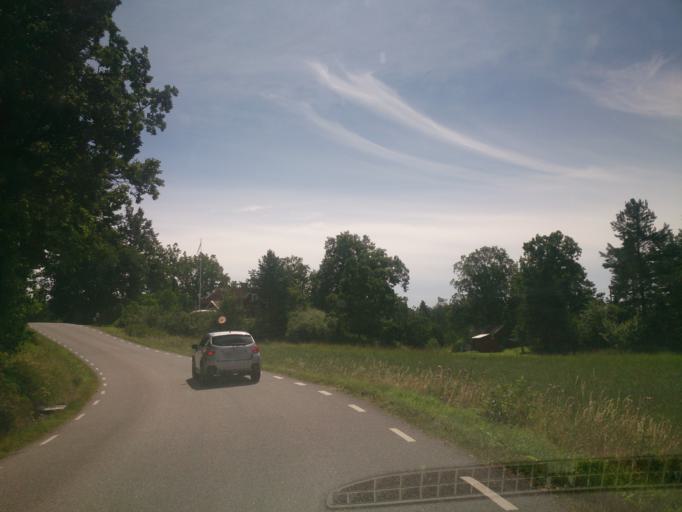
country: SE
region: OEstergoetland
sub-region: Valdemarsviks Kommun
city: Valdemarsvik
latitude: 58.2721
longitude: 16.7077
